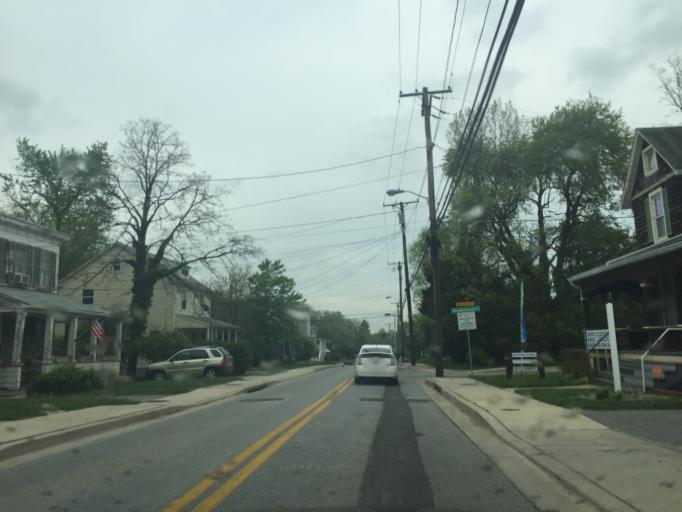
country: US
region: Maryland
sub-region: Baltimore County
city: Catonsville
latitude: 39.2704
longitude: -76.7309
